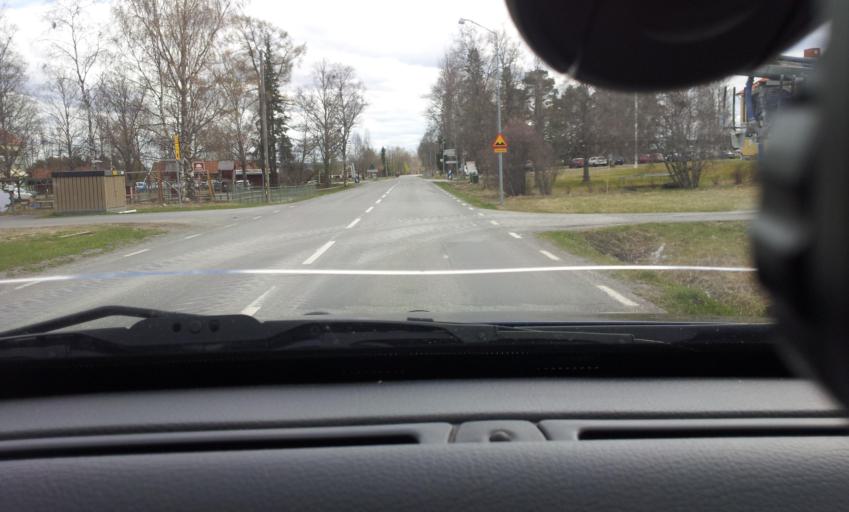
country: SE
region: Jaemtland
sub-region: OEstersunds Kommun
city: Brunflo
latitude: 63.1117
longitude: 14.7311
